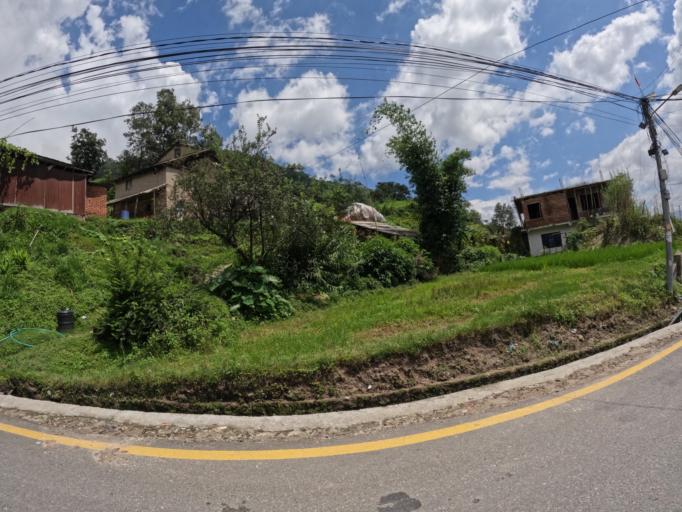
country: NP
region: Central Region
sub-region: Bagmati Zone
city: Kathmandu
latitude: 27.7885
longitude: 85.3299
